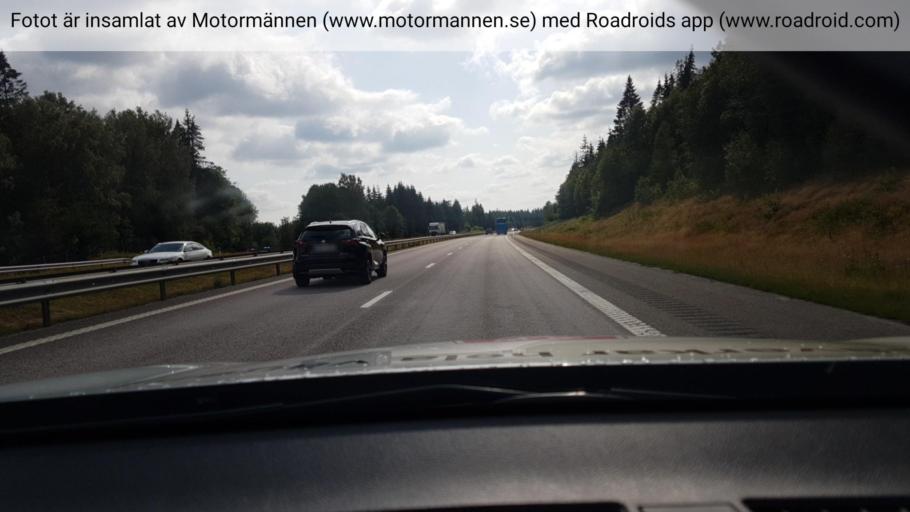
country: SE
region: Vaestra Goetaland
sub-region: Boras Kommun
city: Sandared
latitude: 57.6879
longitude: 12.7893
